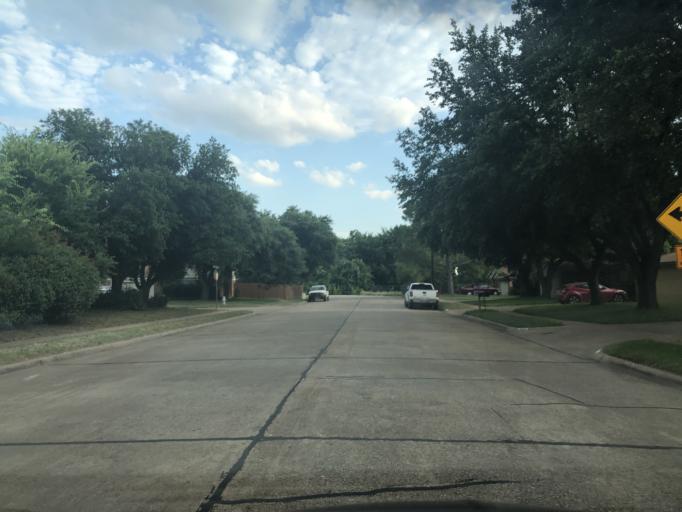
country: US
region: Texas
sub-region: Dallas County
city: Irving
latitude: 32.7921
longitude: -96.9527
